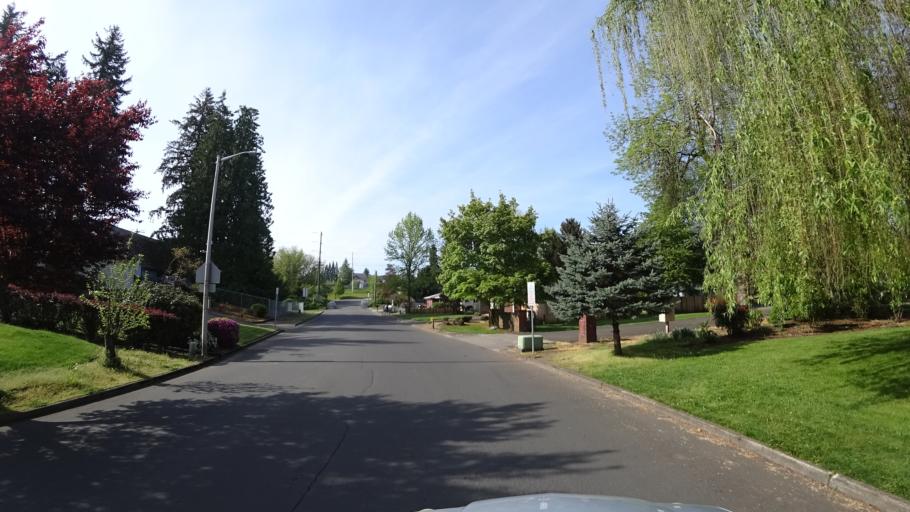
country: US
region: Oregon
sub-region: Washington County
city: Hillsboro
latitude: 45.5228
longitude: -122.9644
